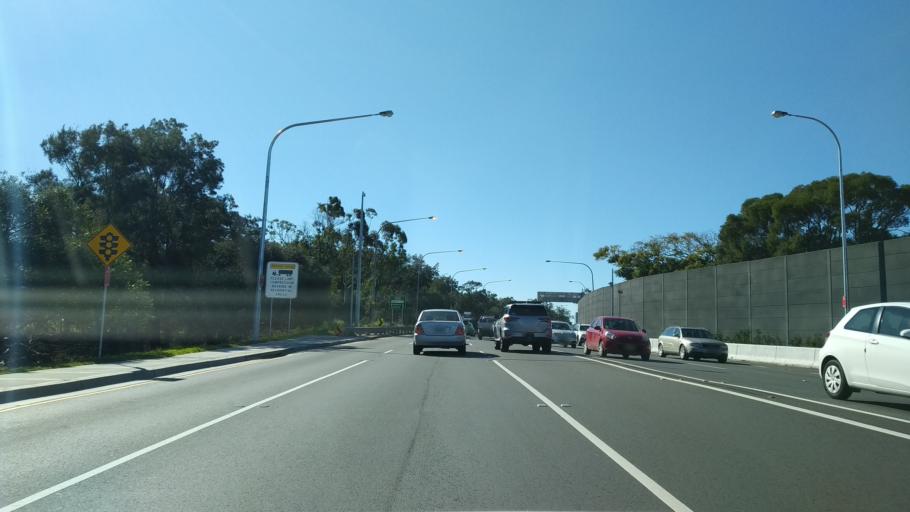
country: AU
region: New South Wales
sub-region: Canada Bay
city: Wareemba
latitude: -33.8727
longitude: 151.1381
